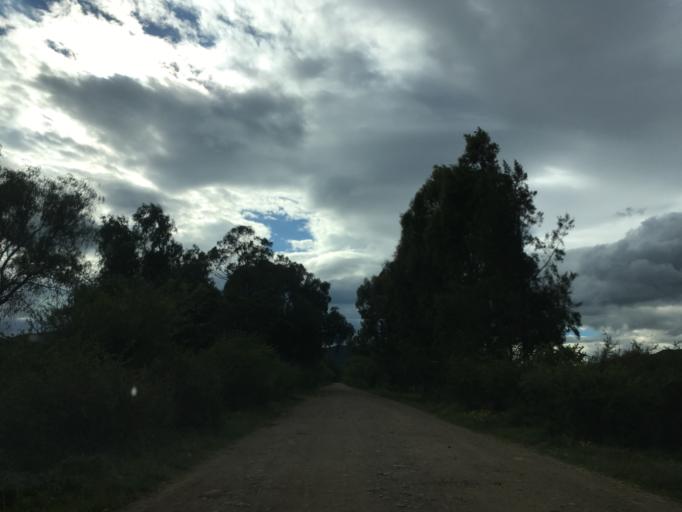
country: MX
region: Guanajuato
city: Iramuco
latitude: 19.9710
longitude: -100.9500
